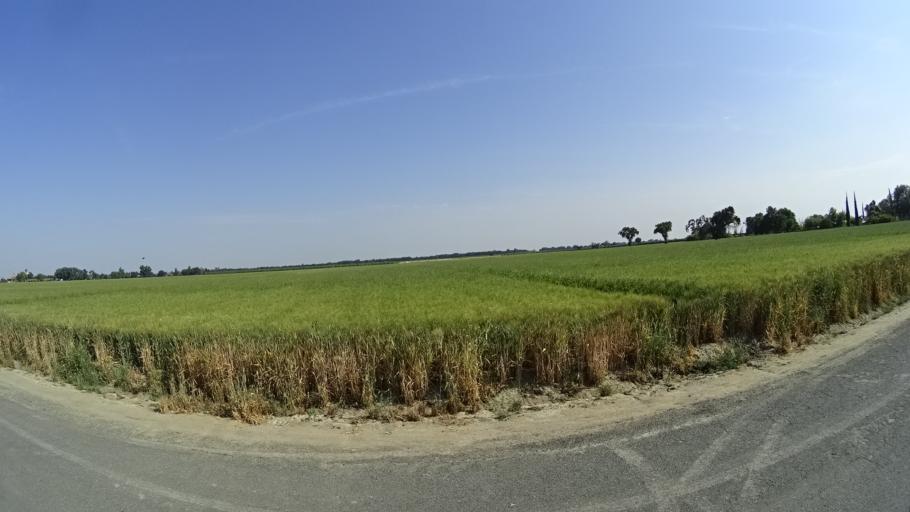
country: US
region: California
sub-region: Kings County
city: Lemoore
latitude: 36.3206
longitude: -119.8379
